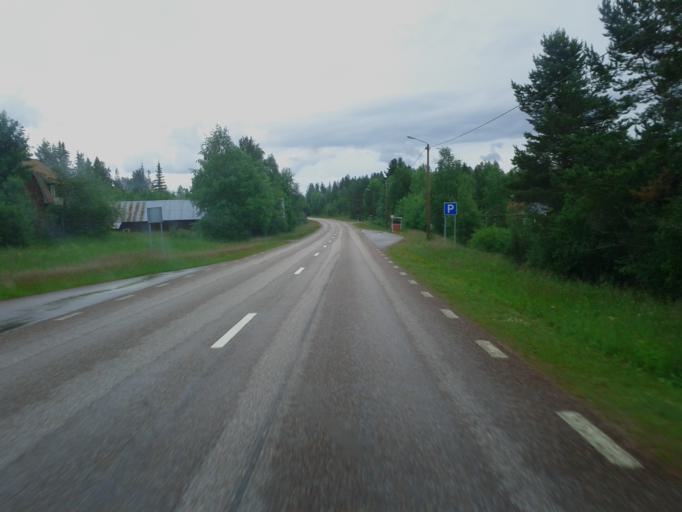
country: NO
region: Hedmark
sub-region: Trysil
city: Innbygda
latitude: 61.7257
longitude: 12.9934
